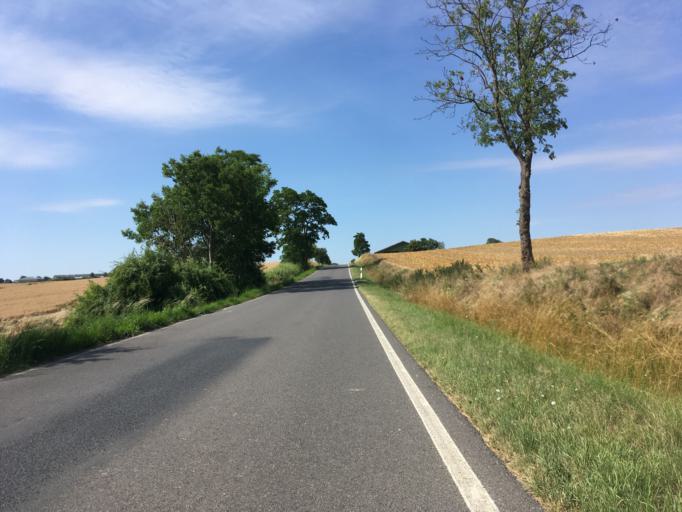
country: DE
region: Brandenburg
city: Gramzow
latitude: 53.2505
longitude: 14.0537
